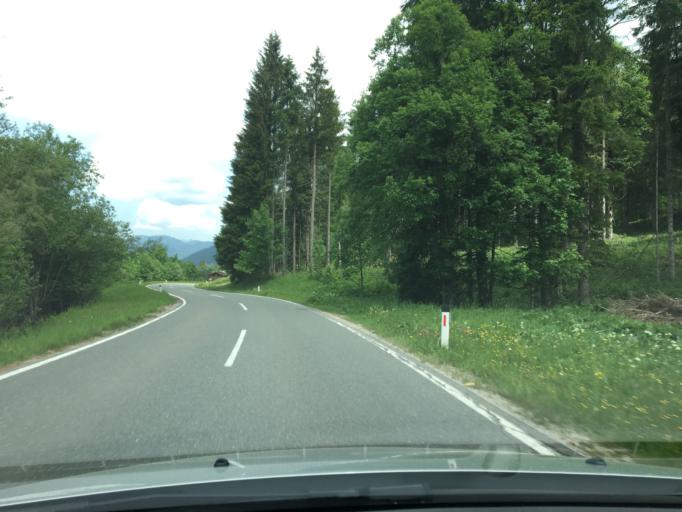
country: AT
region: Salzburg
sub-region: Politischer Bezirk Sankt Johann im Pongau
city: Kleinarl
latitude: 47.2516
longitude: 13.3275
